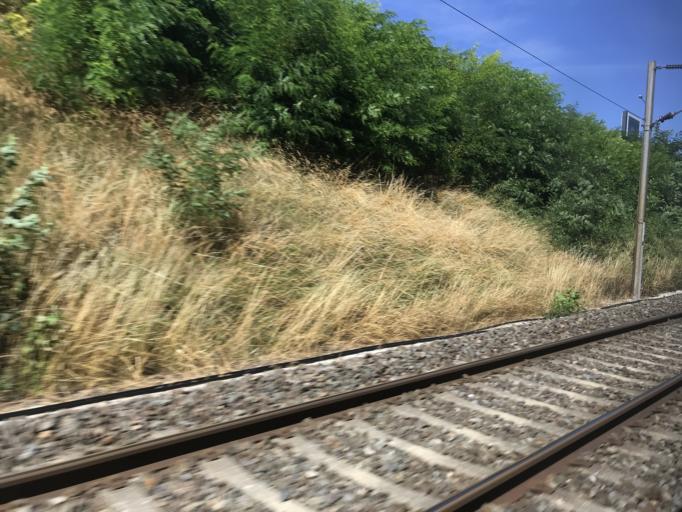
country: FR
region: Champagne-Ardenne
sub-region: Departement de la Marne
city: Reims
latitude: 49.2320
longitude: 4.0242
